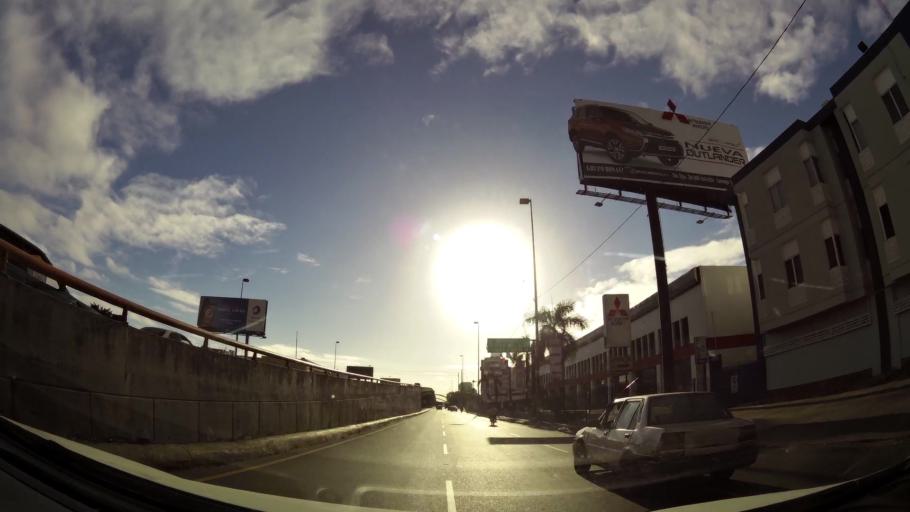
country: DO
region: Nacional
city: La Julia
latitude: 18.4823
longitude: -69.9228
